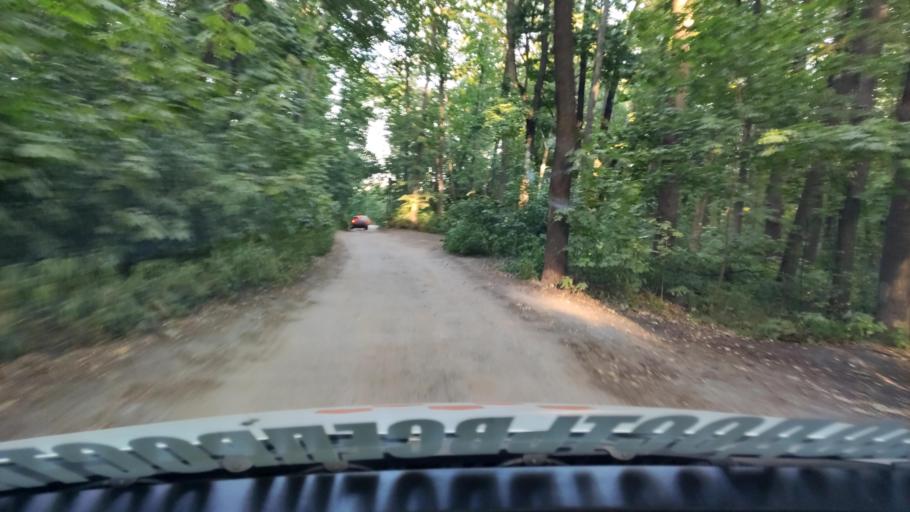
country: RU
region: Voronezj
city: Podgornoye
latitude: 51.7430
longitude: 39.2244
